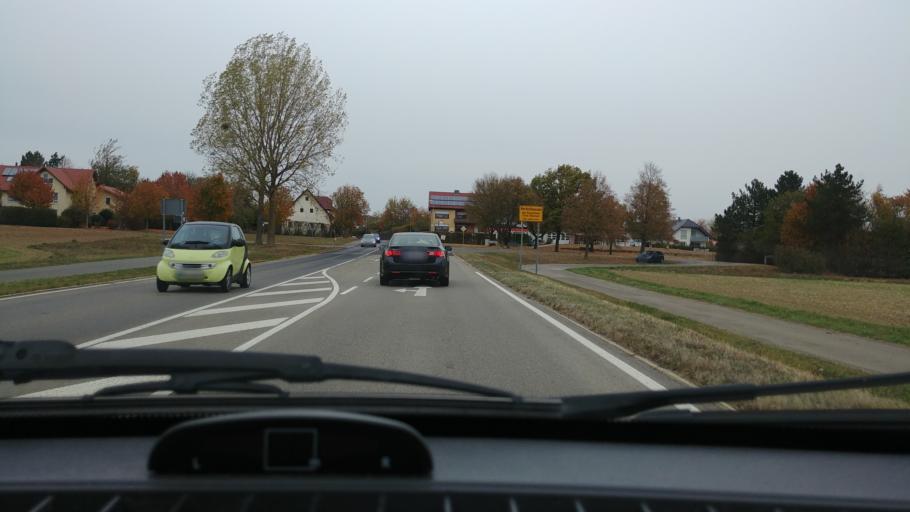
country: DE
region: Baden-Wuerttemberg
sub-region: Regierungsbezirk Stuttgart
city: Mulfingen
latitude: 49.4019
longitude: 9.8323
